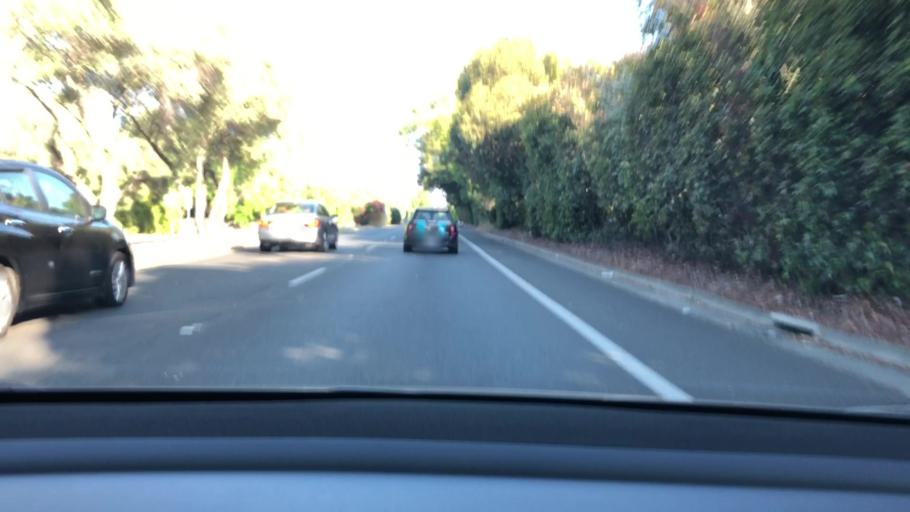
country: US
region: California
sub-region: Santa Clara County
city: Los Altos
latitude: 37.3689
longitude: -122.1088
